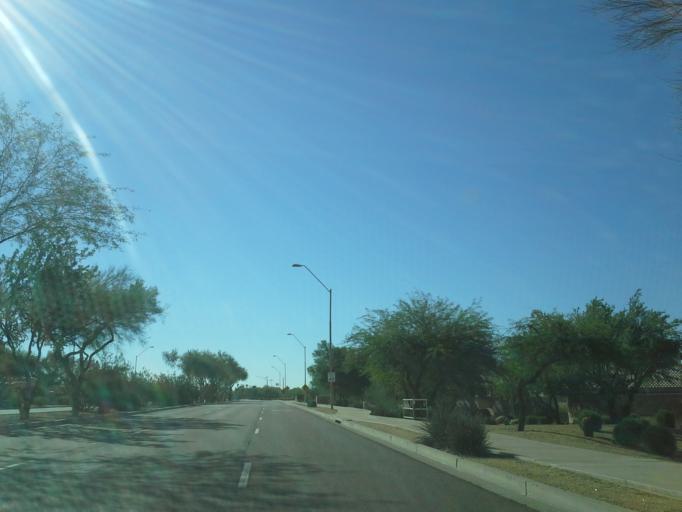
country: US
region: Arizona
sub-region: Maricopa County
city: Scottsdale
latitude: 33.6161
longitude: -111.8706
